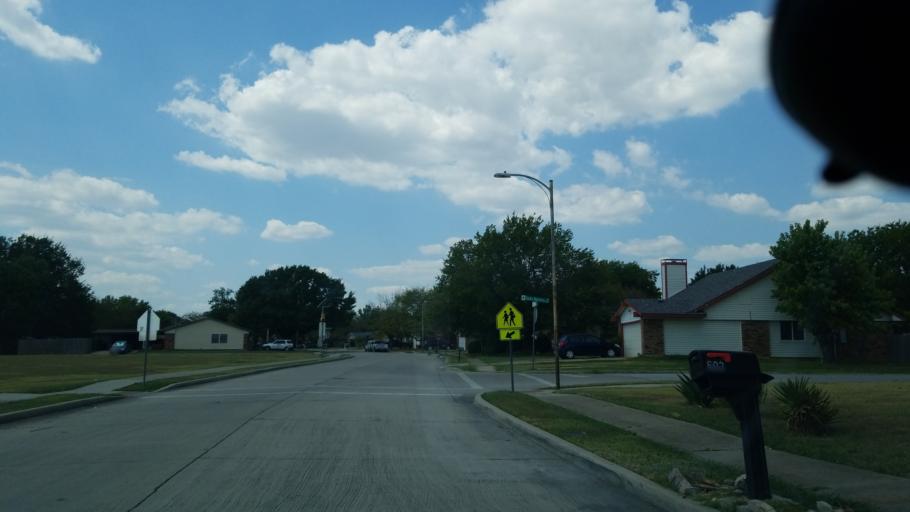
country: US
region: Texas
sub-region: Dallas County
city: Grand Prairie
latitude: 32.7041
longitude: -96.9978
